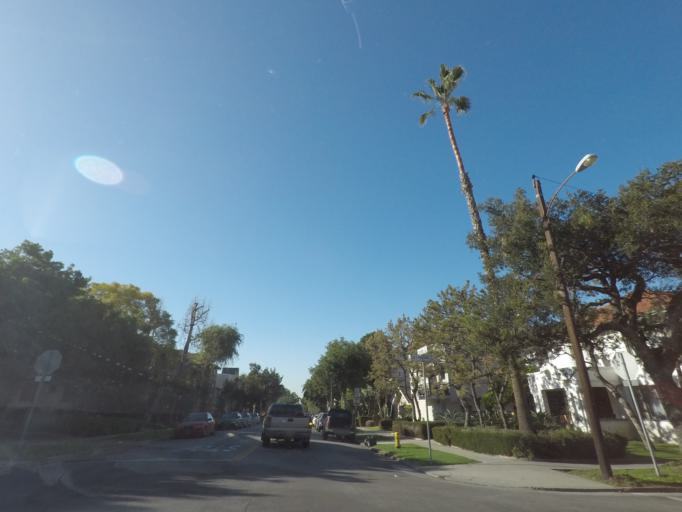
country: US
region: California
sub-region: Los Angeles County
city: Glendale
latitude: 34.1519
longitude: -118.2528
